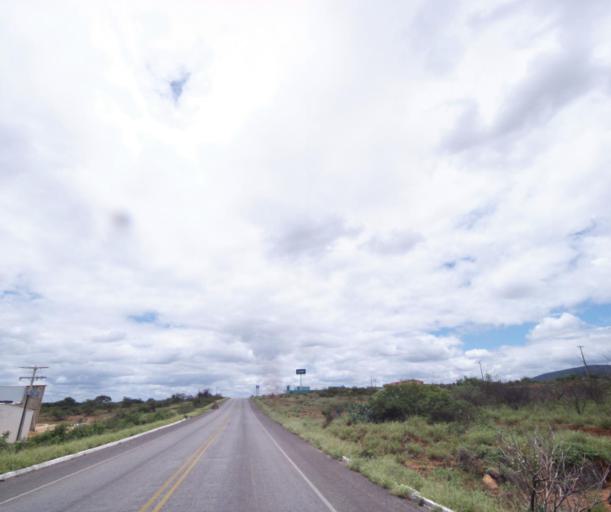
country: BR
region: Bahia
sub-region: Brumado
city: Brumado
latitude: -14.2252
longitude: -41.6733
